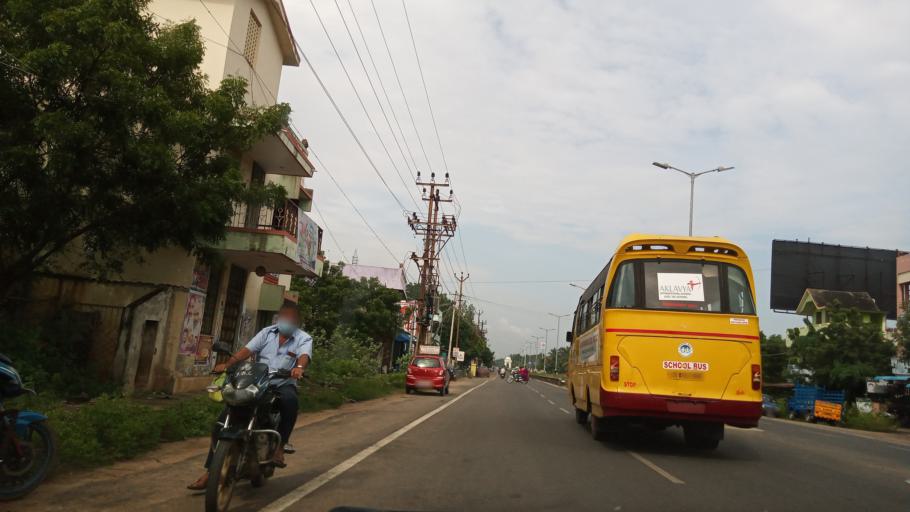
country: IN
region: Tamil Nadu
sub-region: Villupuram
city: Auroville
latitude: 12.0357
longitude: 79.8660
